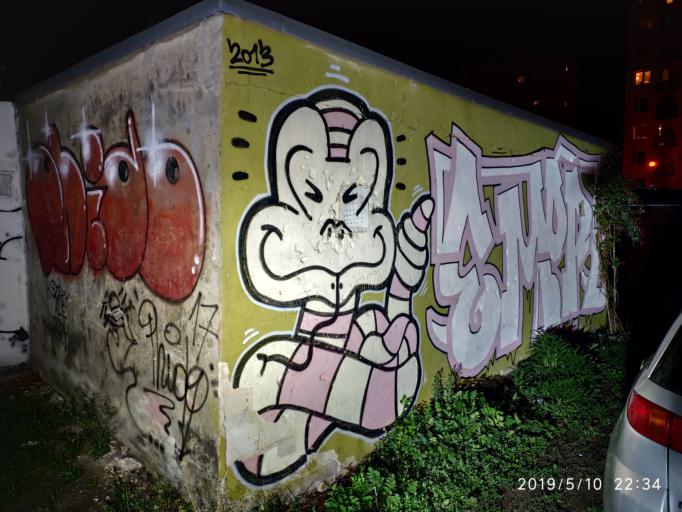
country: PL
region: Lubusz
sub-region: Zielona Gora
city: Zielona Gora
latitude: 51.9346
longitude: 15.4946
